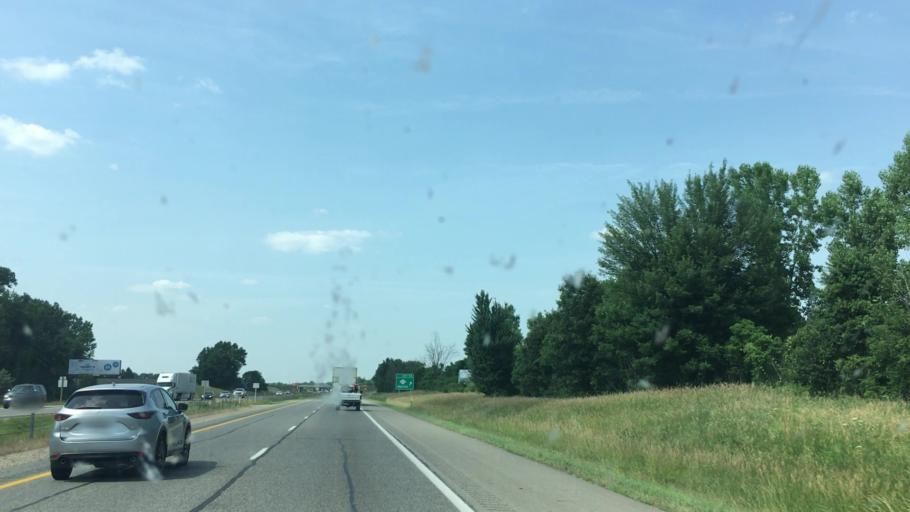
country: US
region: Michigan
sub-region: Allegan County
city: Otsego
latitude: 42.5299
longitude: -85.6585
